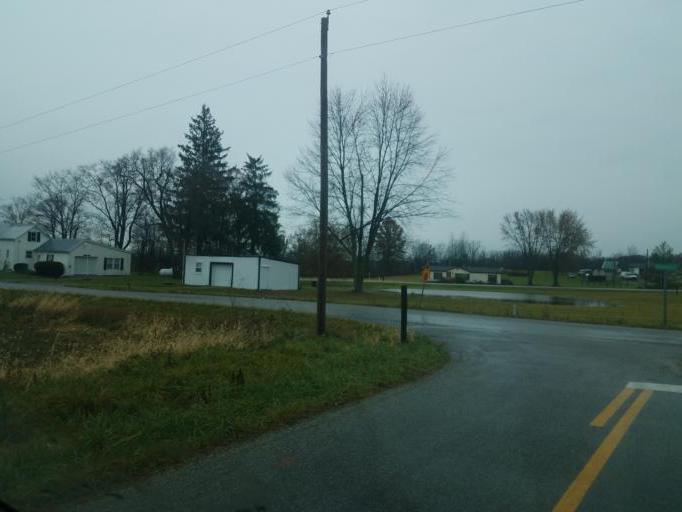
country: US
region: Ohio
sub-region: Knox County
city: Centerburg
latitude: 40.3507
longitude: -82.7746
